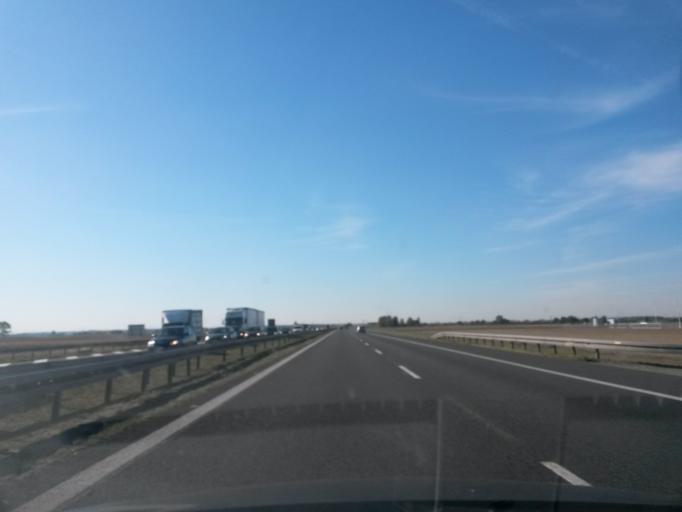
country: PL
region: Opole Voivodeship
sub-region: Powiat brzeski
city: Lewin Brzeski
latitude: 50.7096
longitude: 17.6003
